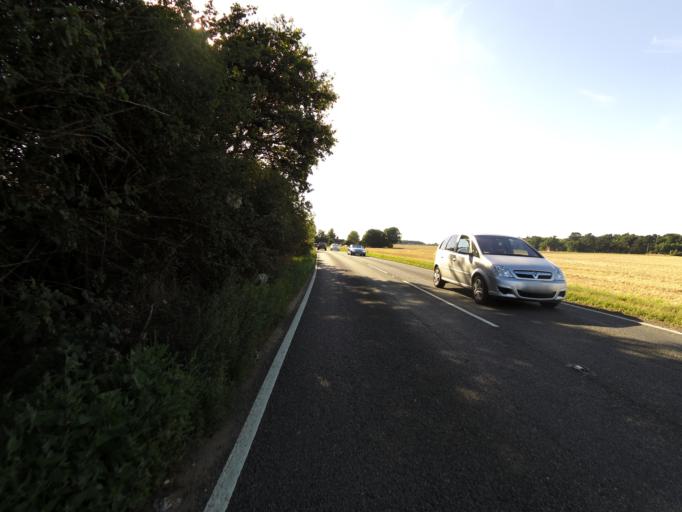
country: GB
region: England
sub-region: Suffolk
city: Kesgrave
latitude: 52.0504
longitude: 1.2585
